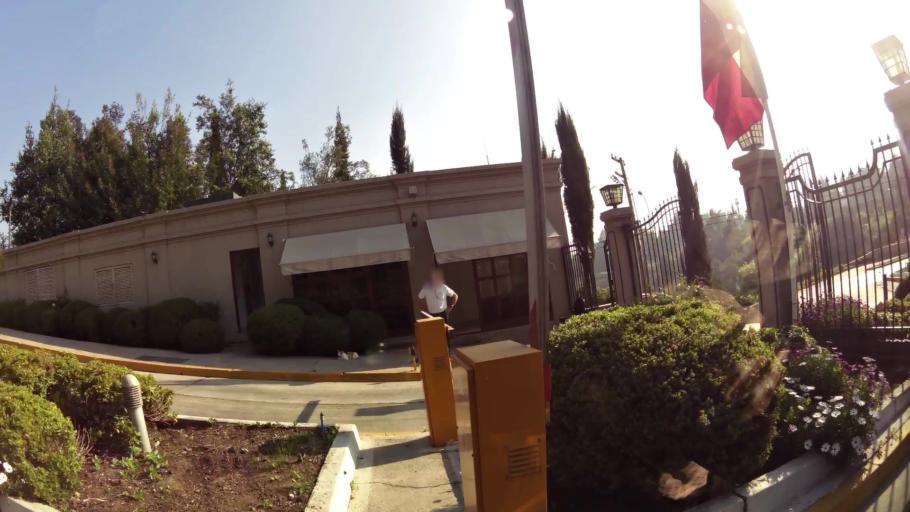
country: CL
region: Santiago Metropolitan
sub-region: Provincia de Santiago
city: Villa Presidente Frei, Nunoa, Santiago, Chile
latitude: -33.3678
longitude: -70.5439
